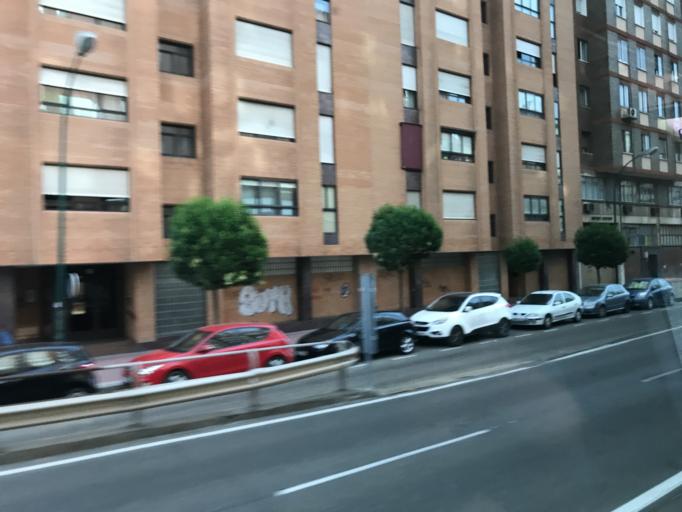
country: ES
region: Castille and Leon
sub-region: Provincia de Valladolid
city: Valladolid
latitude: 41.6388
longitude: -4.7306
